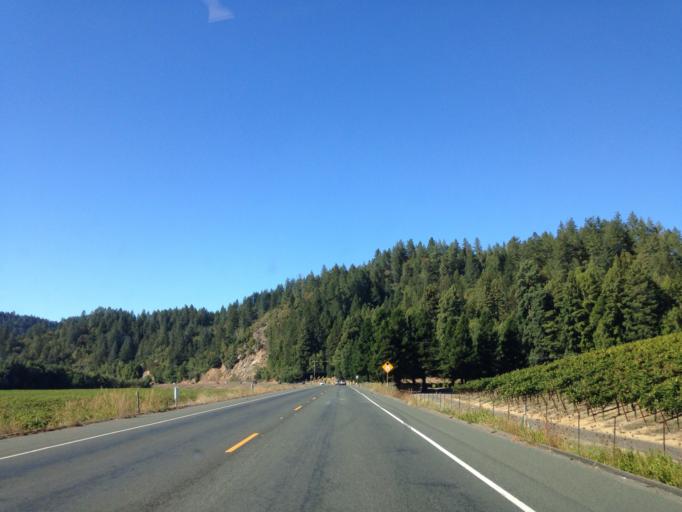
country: US
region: California
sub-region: Sonoma County
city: Guerneville
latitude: 38.5131
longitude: -122.9670
